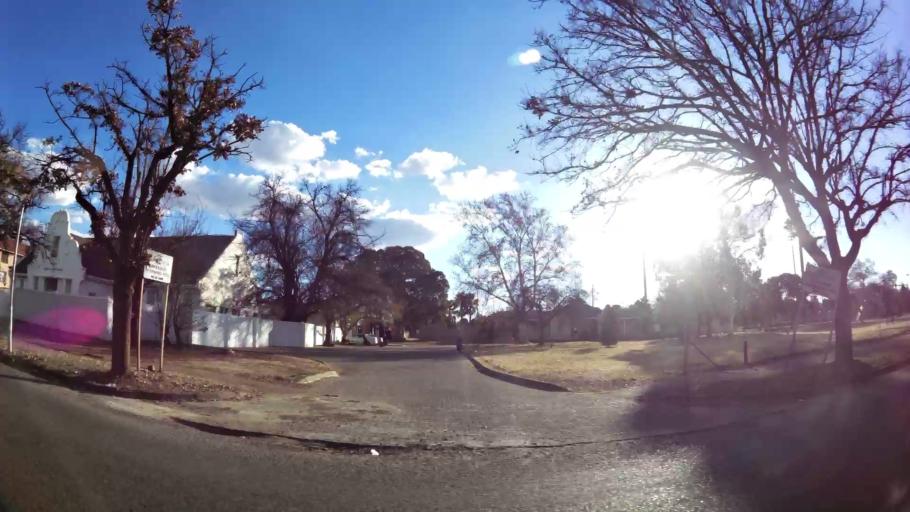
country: ZA
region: North-West
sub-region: Dr Kenneth Kaunda District Municipality
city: Potchefstroom
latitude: -26.7130
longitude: 27.0910
